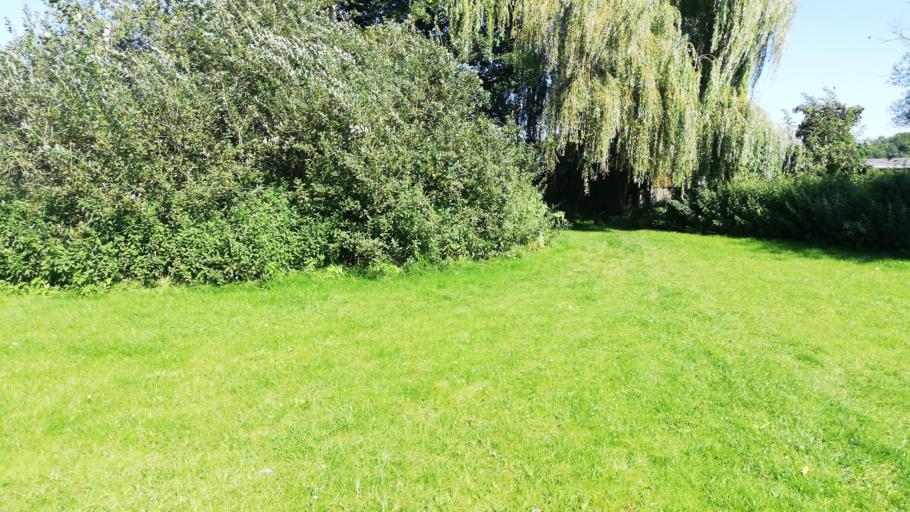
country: DE
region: Brandenburg
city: Wittstock
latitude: 53.1797
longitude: 12.6316
